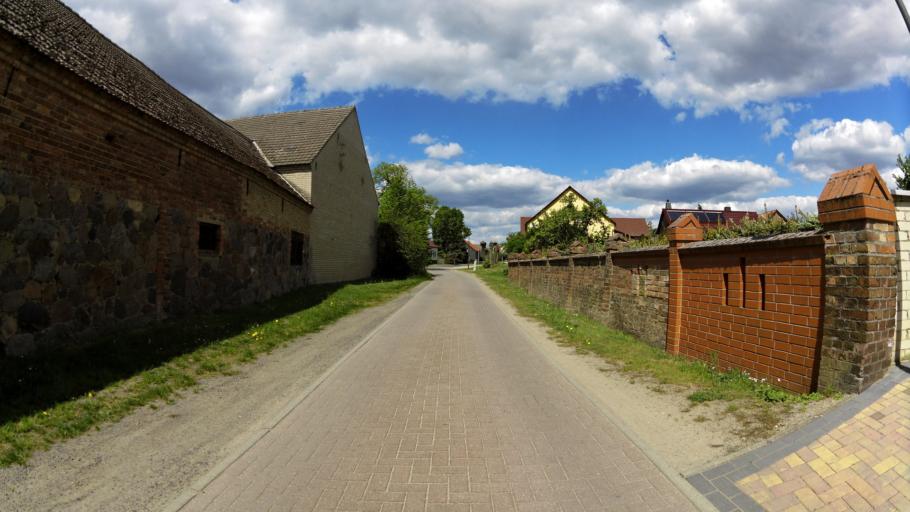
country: DE
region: Brandenburg
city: Rietz Neuendorf
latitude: 52.2174
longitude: 14.1240
